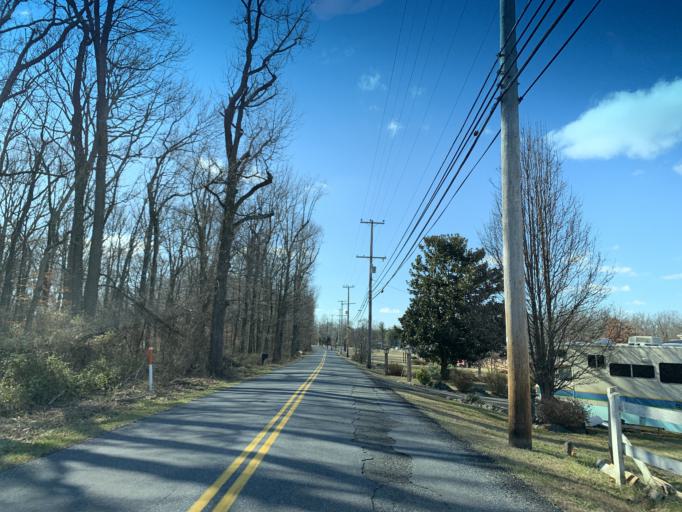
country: US
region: Maryland
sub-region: Harford County
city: Riverside
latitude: 39.4930
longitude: -76.2442
